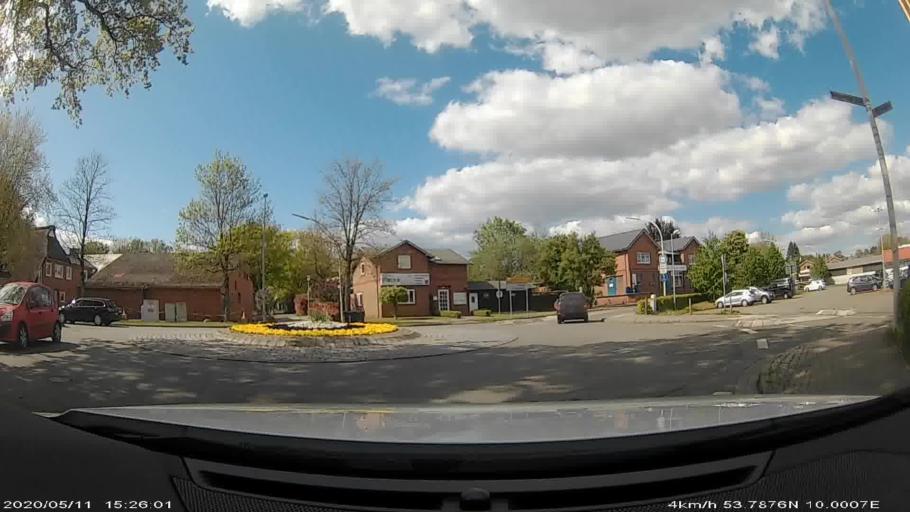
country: DE
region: Schleswig-Holstein
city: Henstedt-Ulzburg
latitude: 53.7815
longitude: 9.9935
